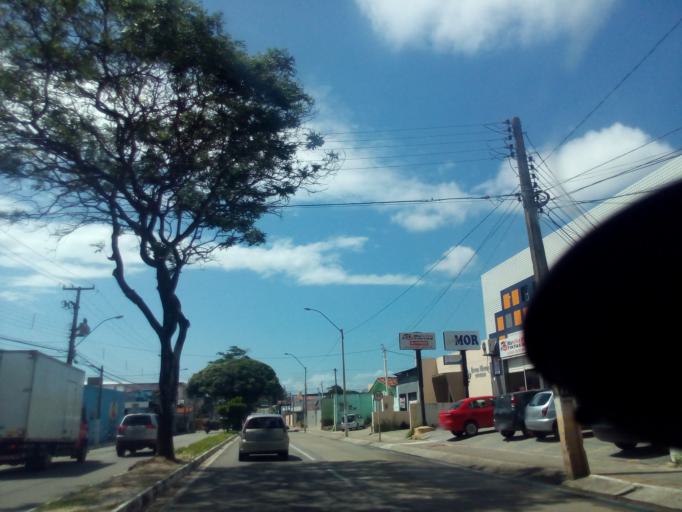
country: BR
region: Rio Grande do Norte
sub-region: Natal
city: Natal
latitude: -5.8261
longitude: -35.2201
